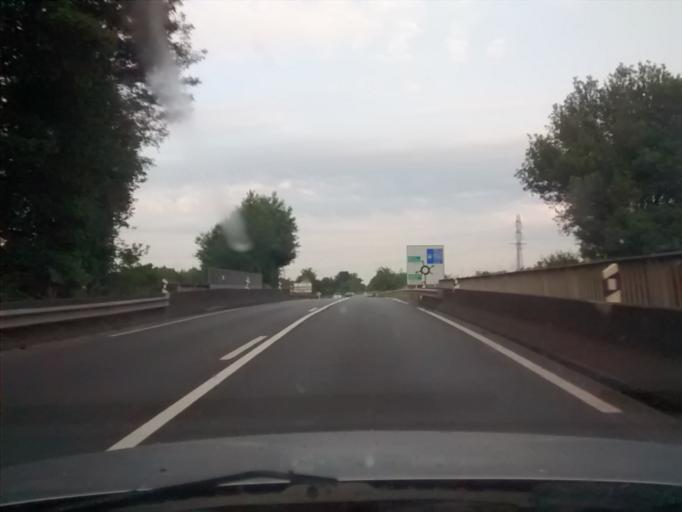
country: FR
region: Pays de la Loire
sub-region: Departement de la Sarthe
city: Champagne
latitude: 48.0103
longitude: 0.3025
